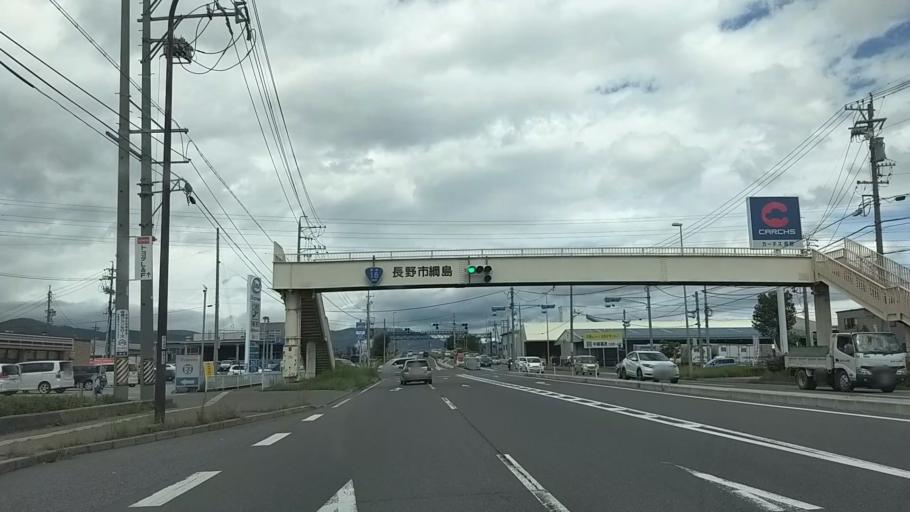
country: JP
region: Nagano
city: Nagano-shi
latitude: 36.6136
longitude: 138.1972
